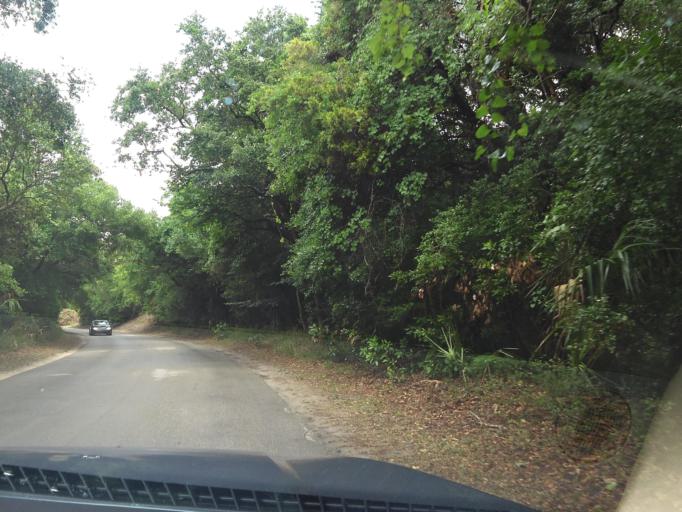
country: US
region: Florida
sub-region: Nassau County
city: Fernandina Beach
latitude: 30.6783
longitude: -81.4343
